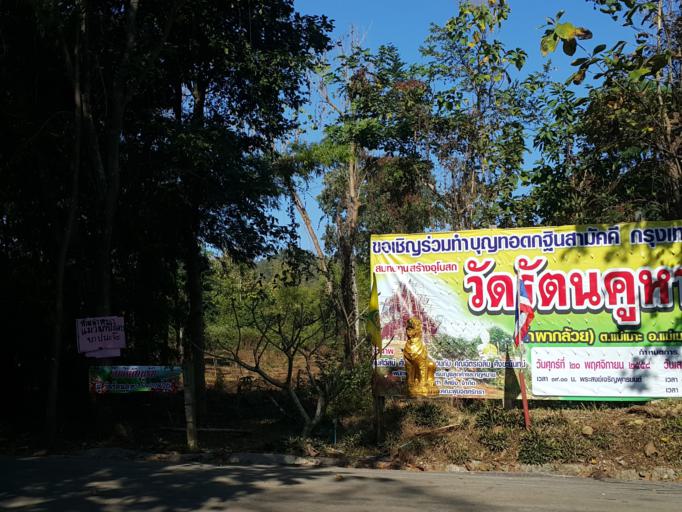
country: TH
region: Lampang
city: Mae Mo
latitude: 18.2950
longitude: 99.6582
